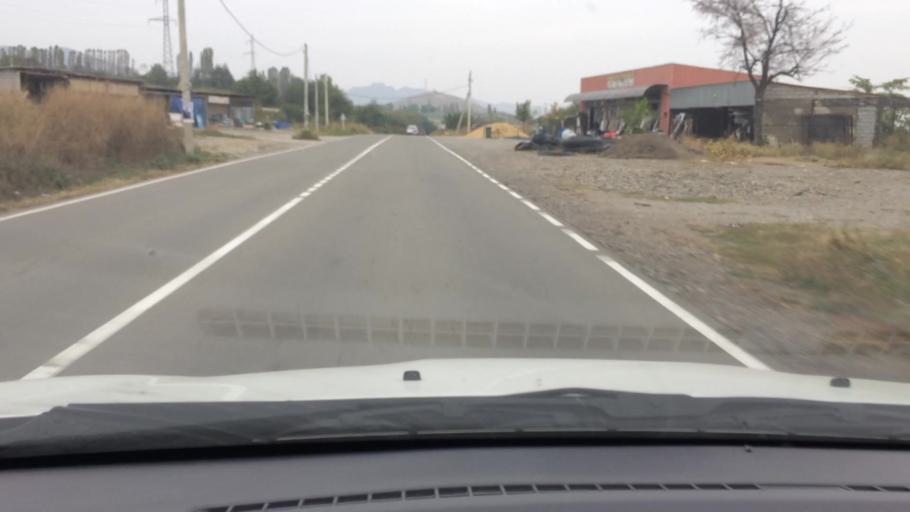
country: AM
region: Tavush
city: Bagratashen
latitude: 41.2668
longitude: 44.7917
